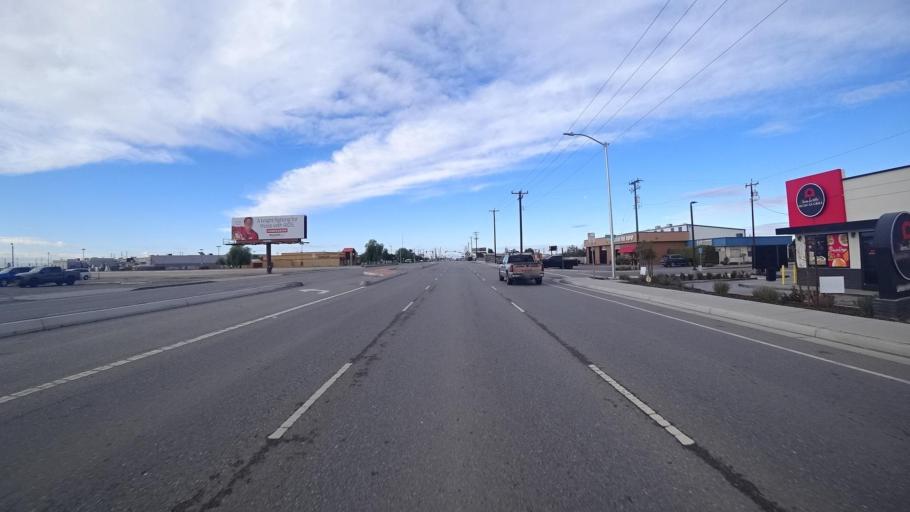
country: US
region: California
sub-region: Kern County
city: Greenacres
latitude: 35.3835
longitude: -119.0867
